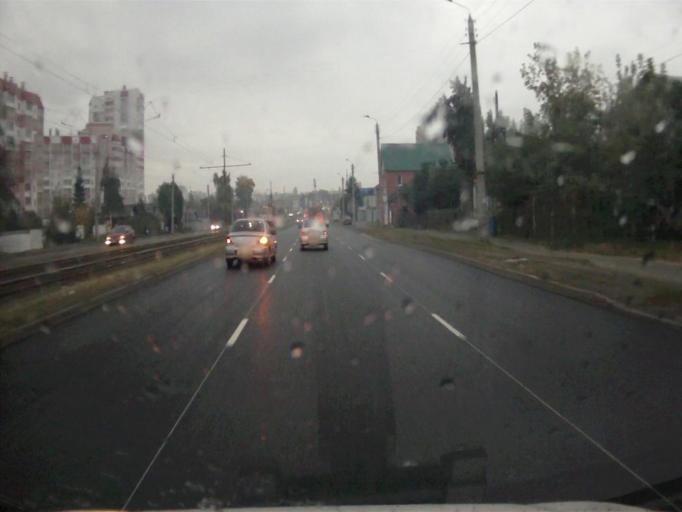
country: RU
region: Chelyabinsk
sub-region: Gorod Chelyabinsk
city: Chelyabinsk
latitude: 55.1838
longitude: 61.3781
